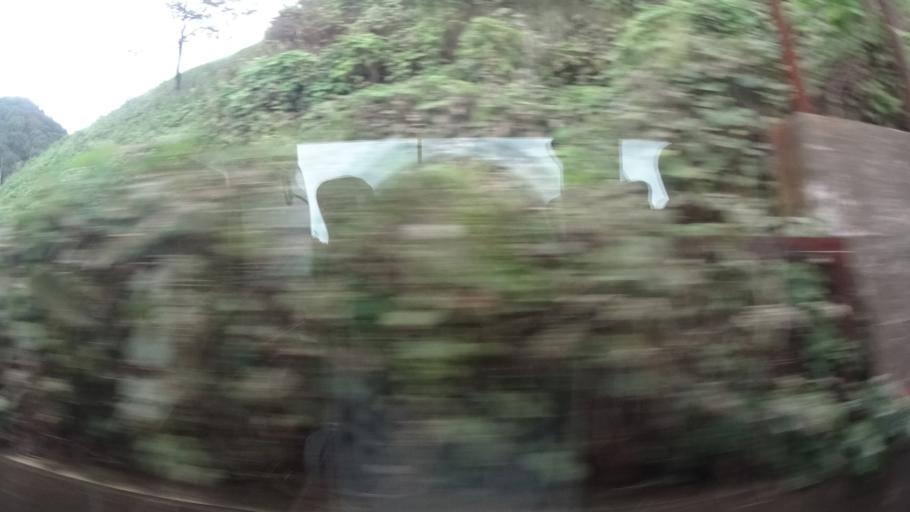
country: JP
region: Niigata
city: Murakami
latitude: 38.4974
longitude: 139.5196
